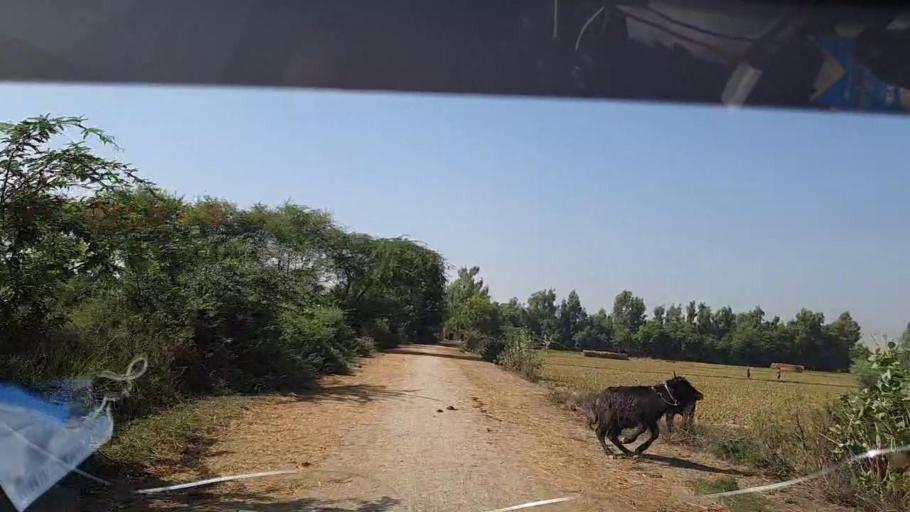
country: PK
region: Sindh
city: Naudero
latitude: 27.6941
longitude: 68.4013
